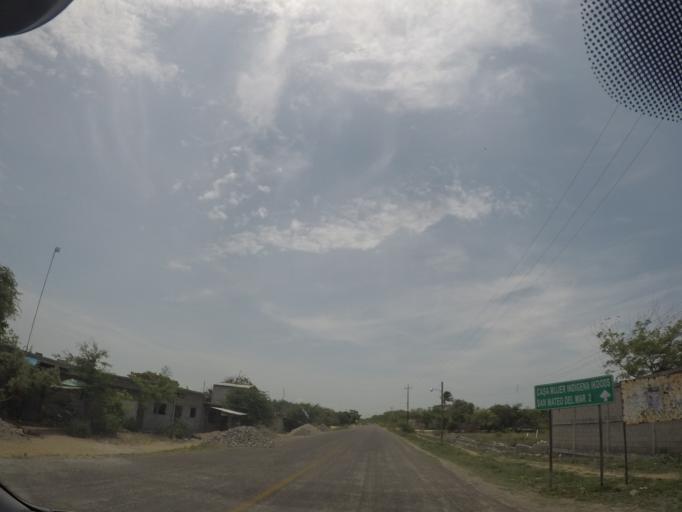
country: MX
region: Oaxaca
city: San Mateo del Mar
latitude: 16.2081
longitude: -95.0022
